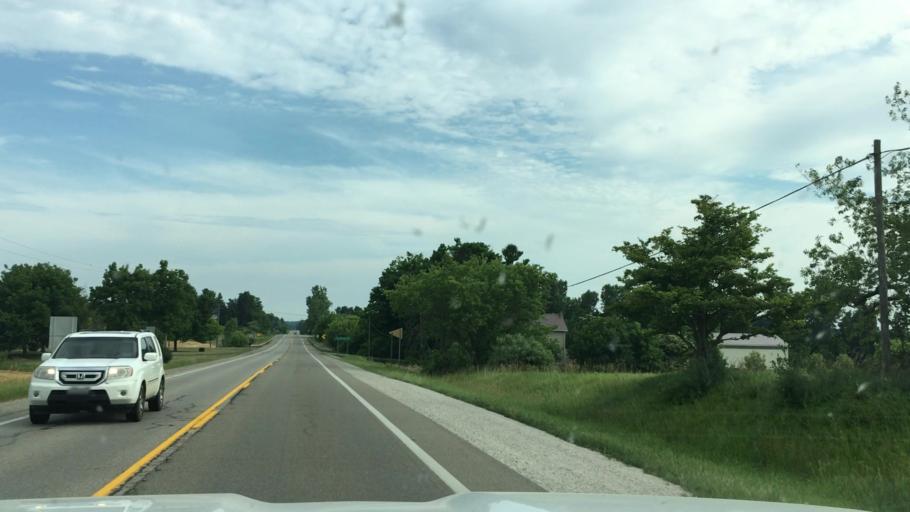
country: US
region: Michigan
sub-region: Sanilac County
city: Brown City
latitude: 43.1850
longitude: -83.0765
